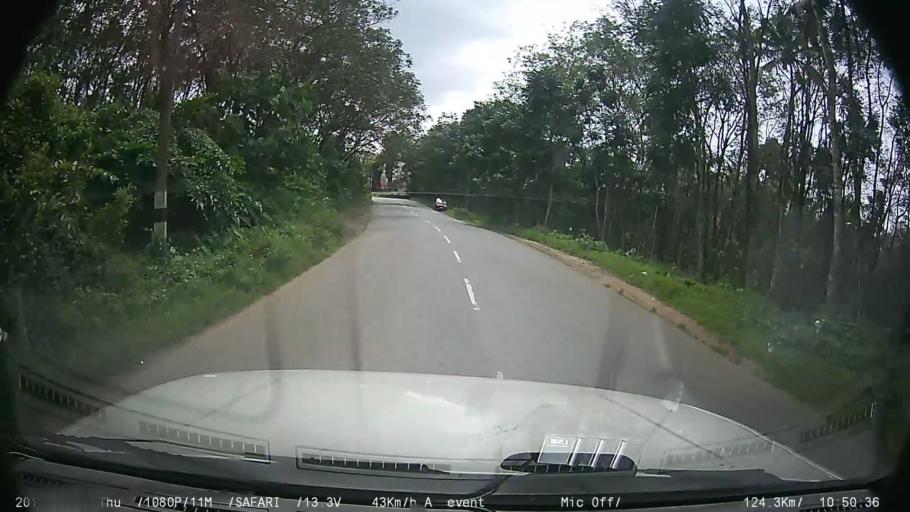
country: IN
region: Kerala
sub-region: Kottayam
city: Palackattumala
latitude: 9.8166
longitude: 76.5854
